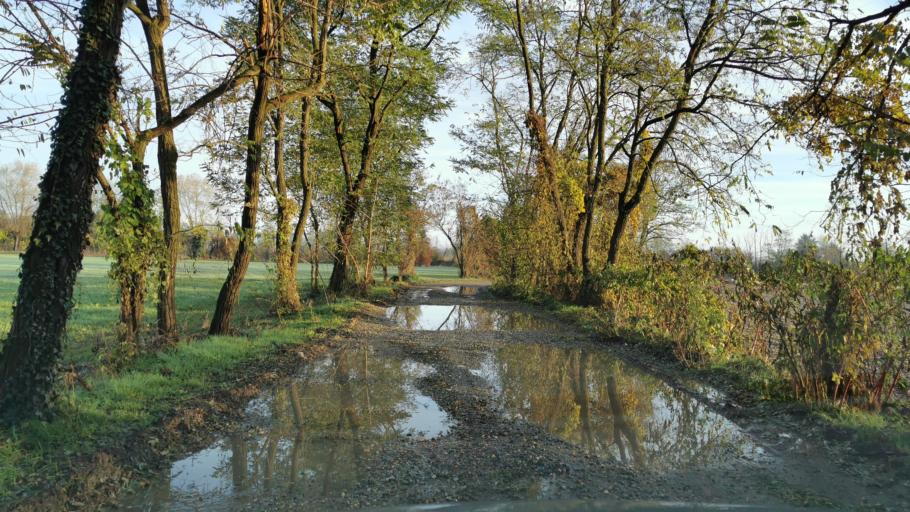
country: IT
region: Piedmont
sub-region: Provincia di Torino
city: San Francesco al Campo
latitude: 45.2044
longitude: 7.6712
